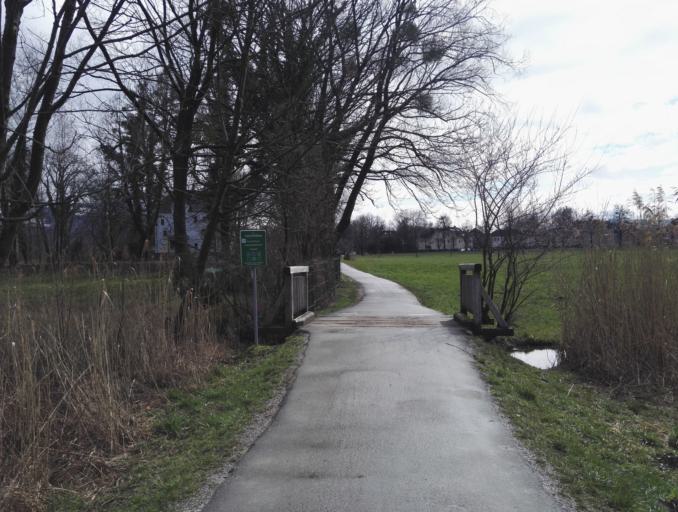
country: AT
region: Salzburg
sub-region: Salzburg Stadt
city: Salzburg
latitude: 47.7881
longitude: 13.0559
